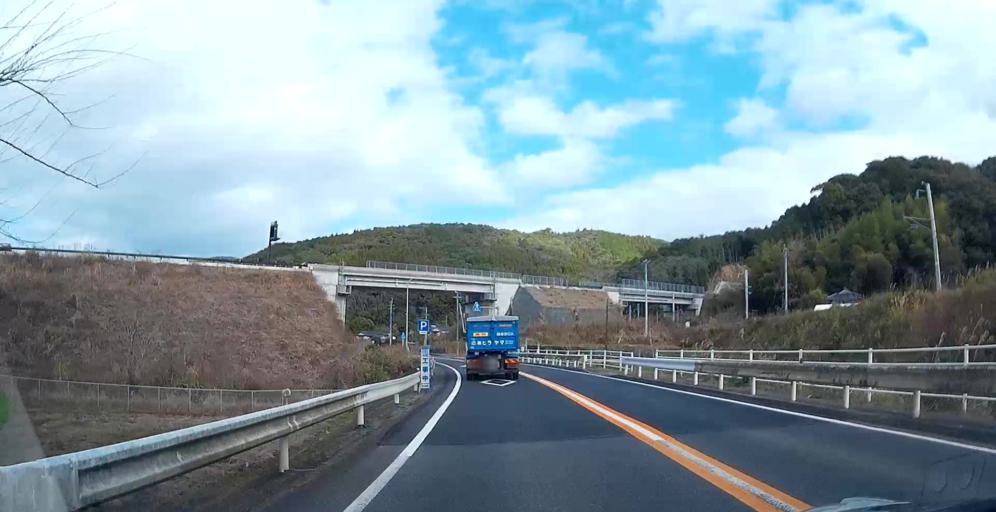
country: JP
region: Kumamoto
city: Minamata
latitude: 32.2268
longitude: 130.4410
